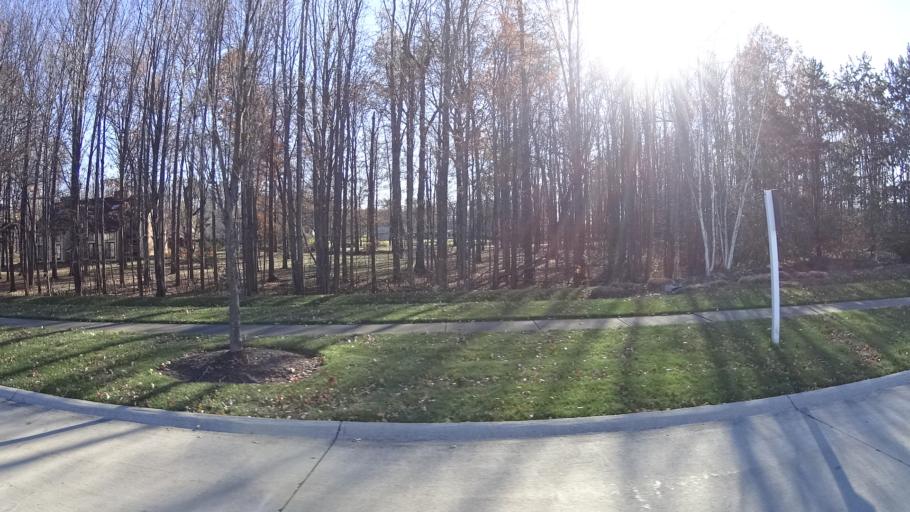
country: US
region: Ohio
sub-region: Lorain County
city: Avon Center
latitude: 41.4365
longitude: -81.9881
